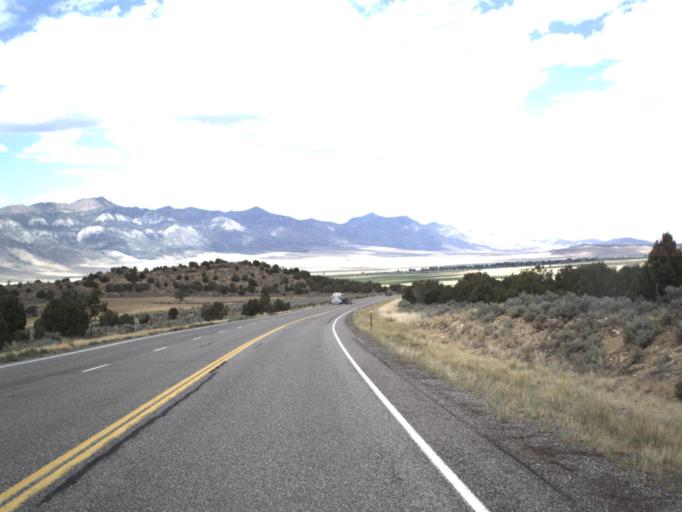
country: US
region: Utah
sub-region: Sanpete County
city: Gunnison
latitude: 39.2003
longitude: -112.0850
